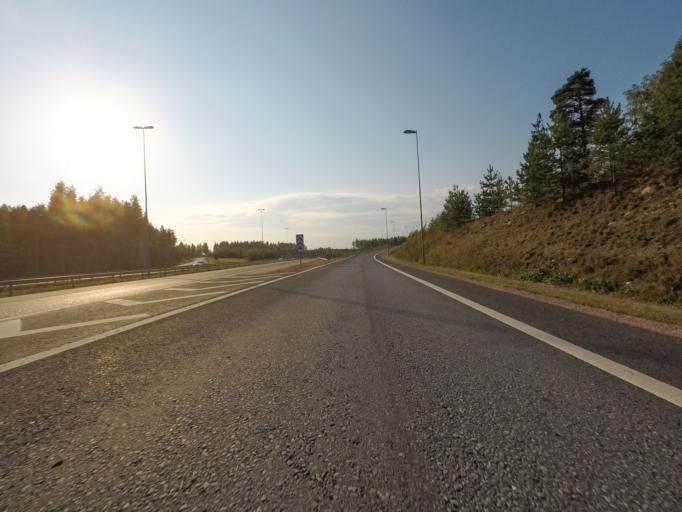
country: FI
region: Uusimaa
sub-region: Helsinki
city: Saukkola
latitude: 60.3415
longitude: 23.9175
